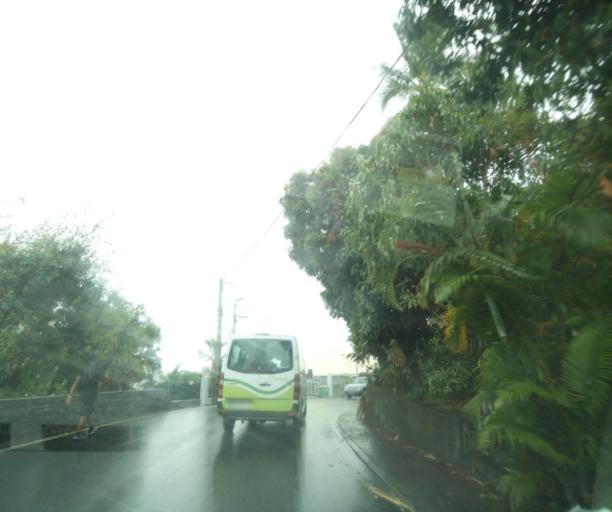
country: RE
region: Reunion
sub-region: Reunion
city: Saint-Paul
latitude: -20.9929
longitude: 55.3302
